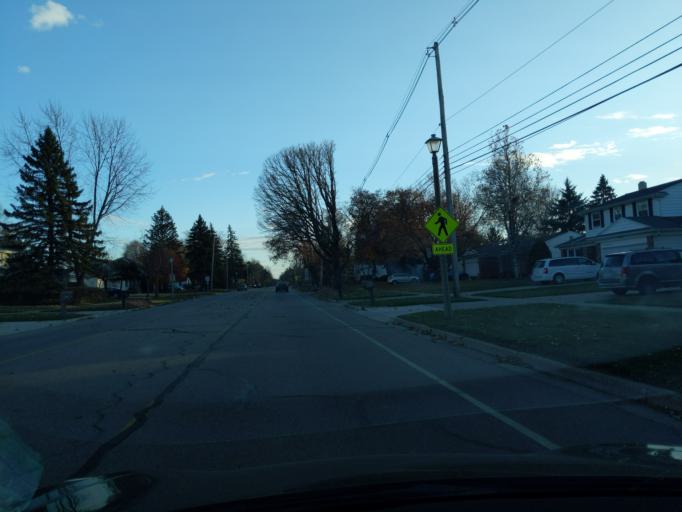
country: US
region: Michigan
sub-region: Ingham County
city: East Lansing
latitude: 42.7568
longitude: -84.4935
